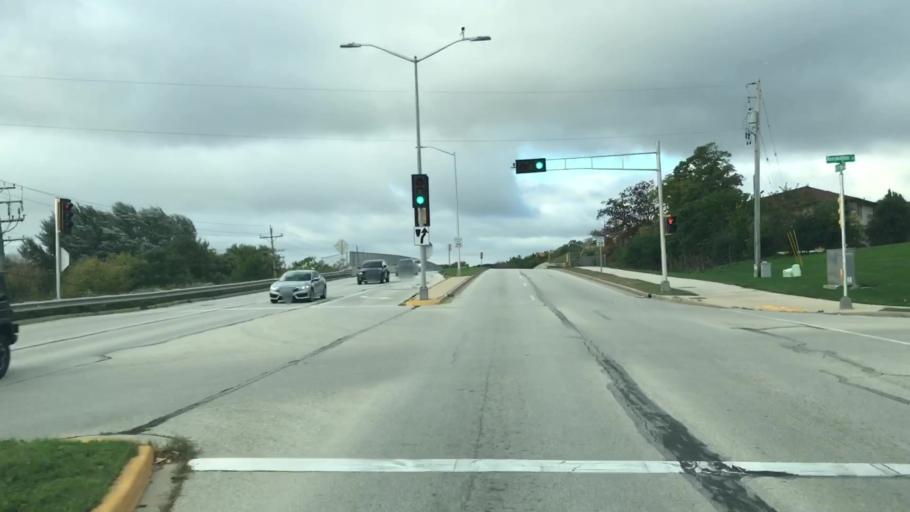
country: US
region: Wisconsin
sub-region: Waukesha County
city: Waukesha
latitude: 43.0013
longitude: -88.2550
